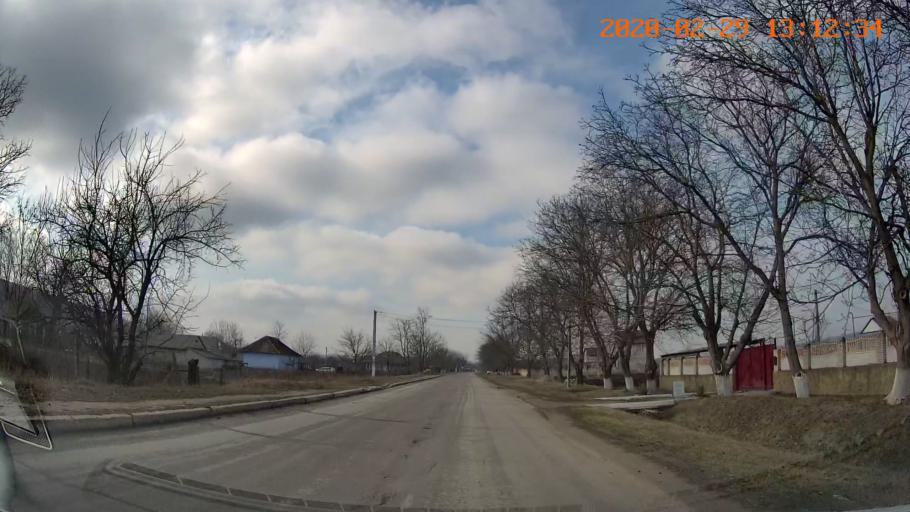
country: MD
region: Telenesti
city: Camenca
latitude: 48.0131
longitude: 28.6942
